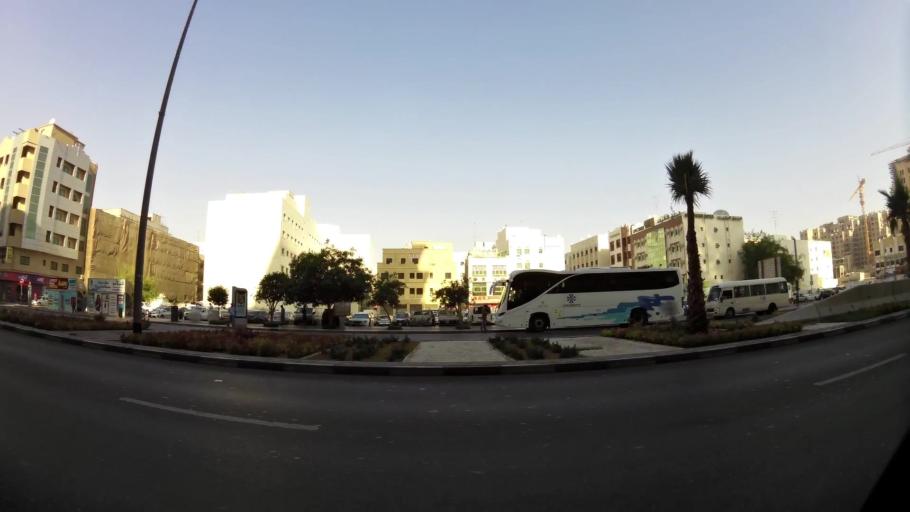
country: AE
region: Ash Shariqah
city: Sharjah
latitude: 25.2685
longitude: 55.3163
